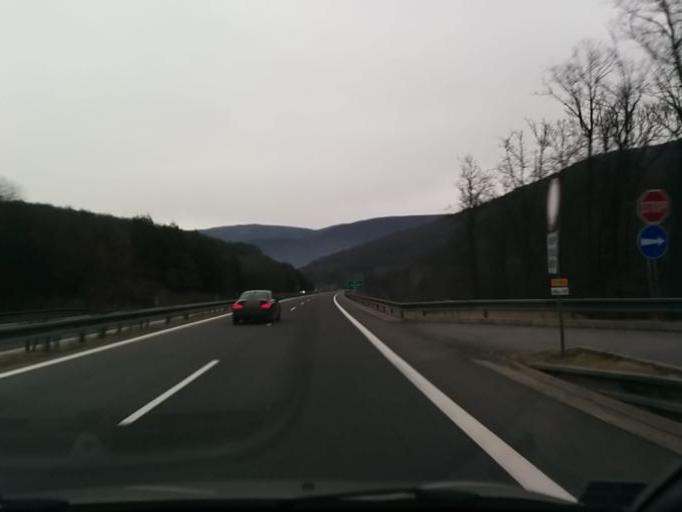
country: SK
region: Nitriansky
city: Tlmace
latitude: 48.3653
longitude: 18.5561
